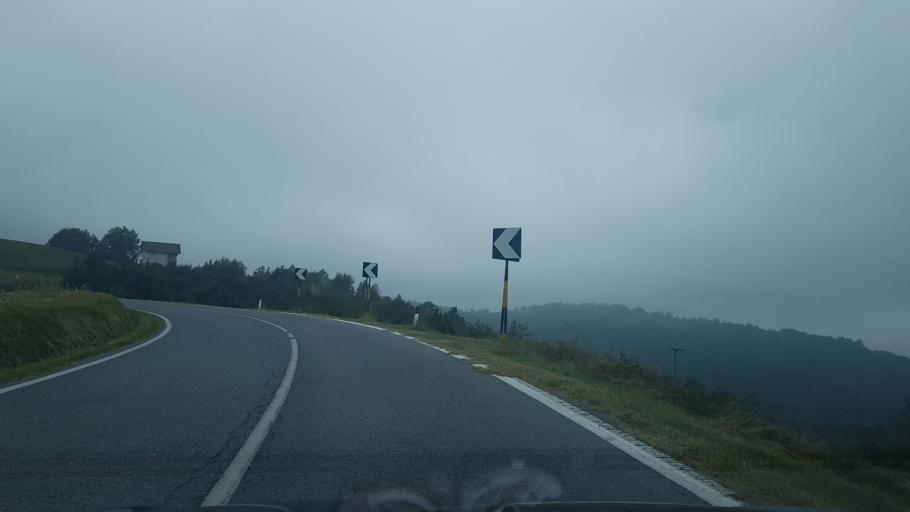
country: IT
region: Piedmont
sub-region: Provincia di Cuneo
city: Paroldo
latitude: 44.4230
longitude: 8.0940
